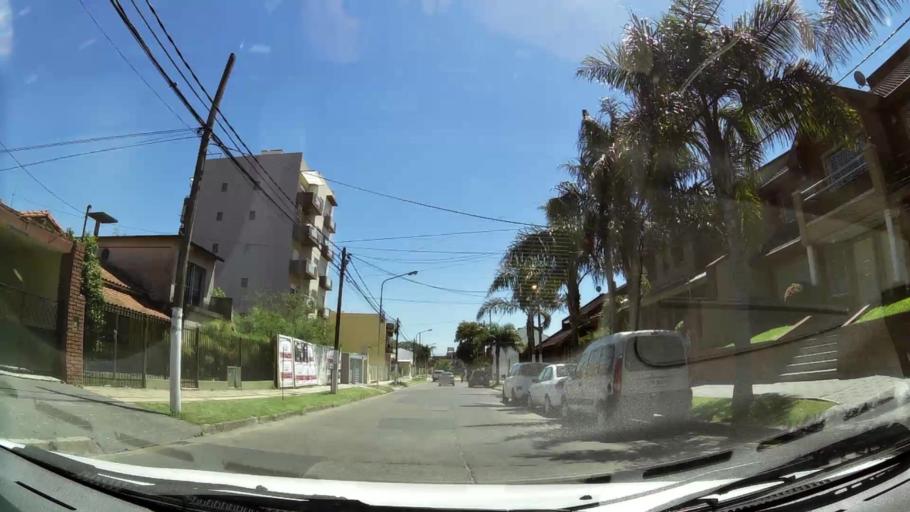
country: AR
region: Buenos Aires
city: Caseros
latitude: -34.5886
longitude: -58.5676
